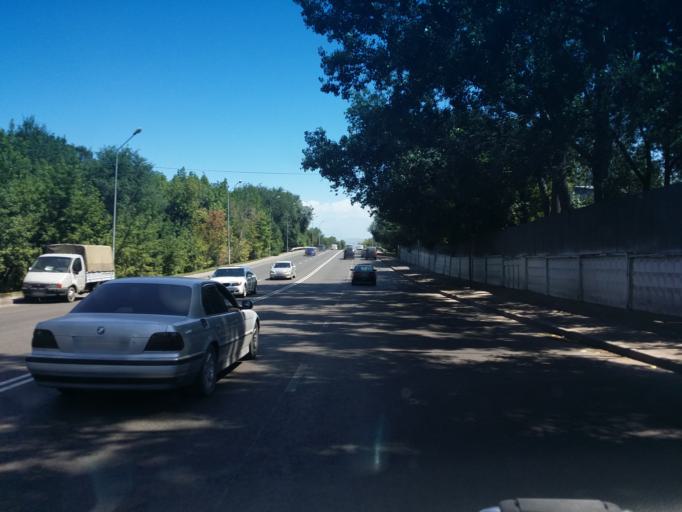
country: KZ
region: Almaty Oblysy
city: Pervomayskiy
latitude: 43.3436
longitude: 76.9748
